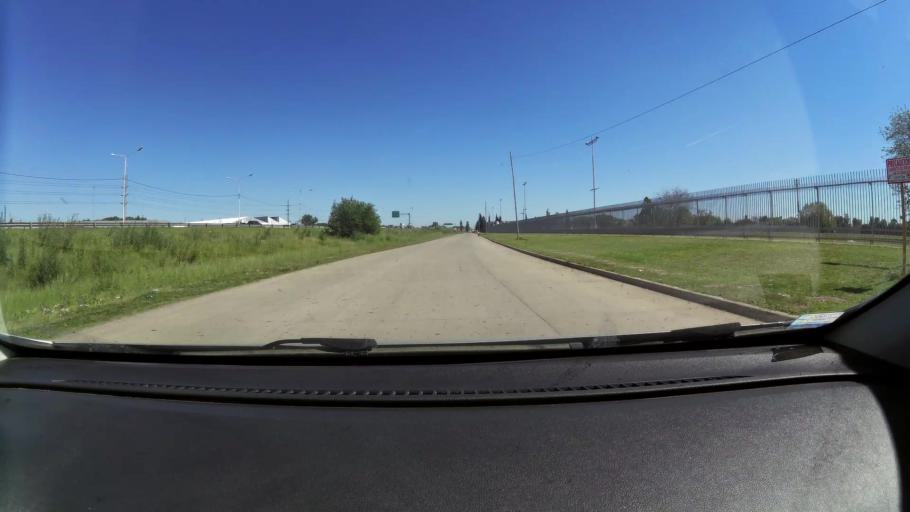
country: AR
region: Santa Fe
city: Perez
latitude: -32.9760
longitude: -60.7132
